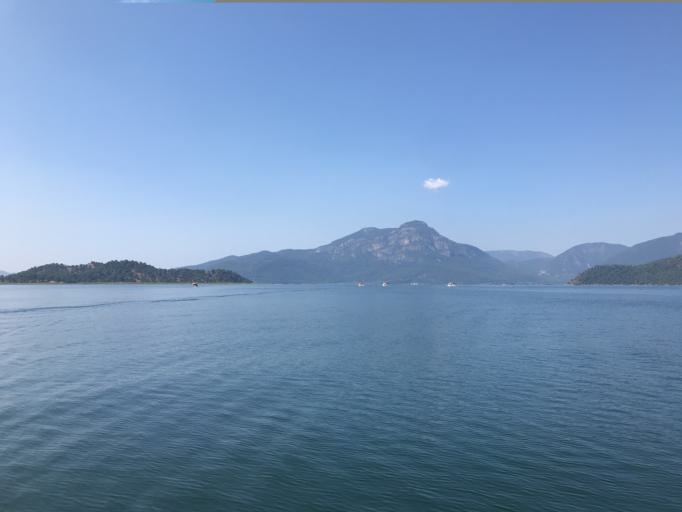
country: TR
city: Dalyan
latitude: 36.9129
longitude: 28.6549
